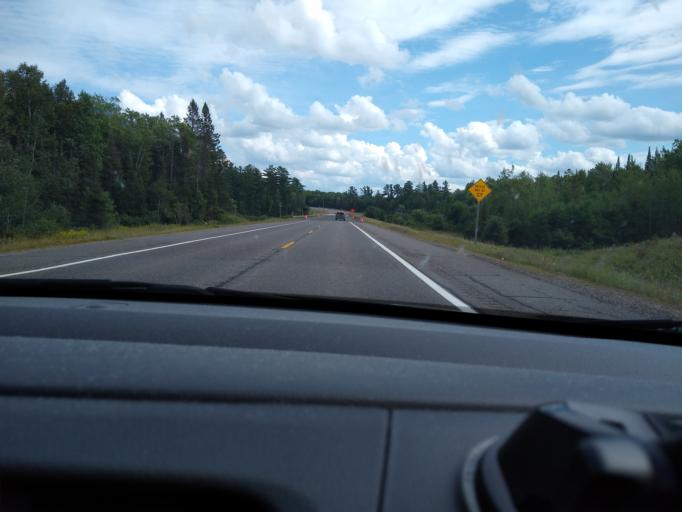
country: US
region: Michigan
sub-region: Marquette County
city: West Ishpeming
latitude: 46.5309
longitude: -88.0058
